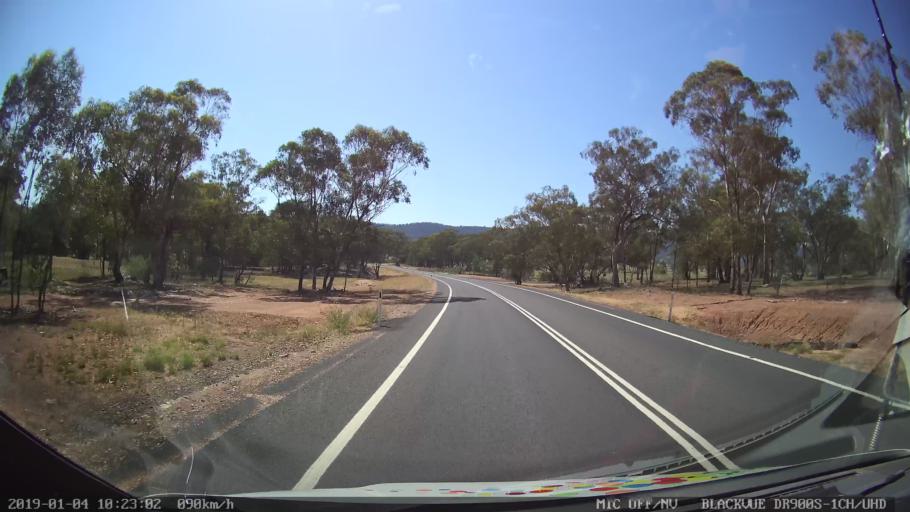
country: AU
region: New South Wales
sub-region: Cabonne
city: Canowindra
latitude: -33.3711
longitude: 148.5336
